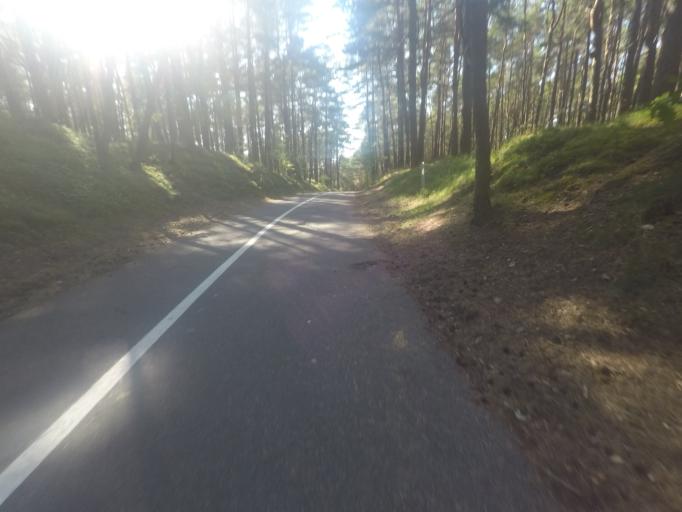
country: LT
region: Klaipedos apskritis
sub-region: Klaipeda
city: Klaipeda
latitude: 55.5464
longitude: 21.1118
